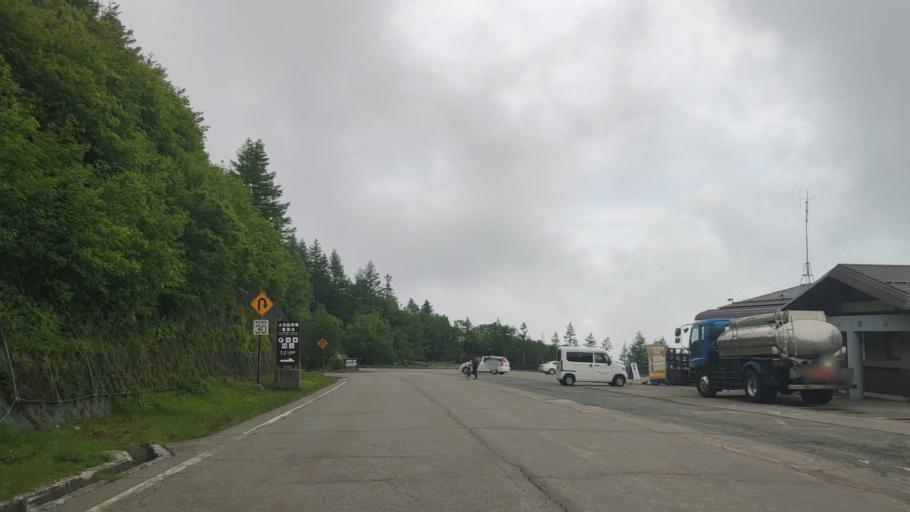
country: JP
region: Yamanashi
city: Fujikawaguchiko
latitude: 35.3746
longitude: 138.6929
